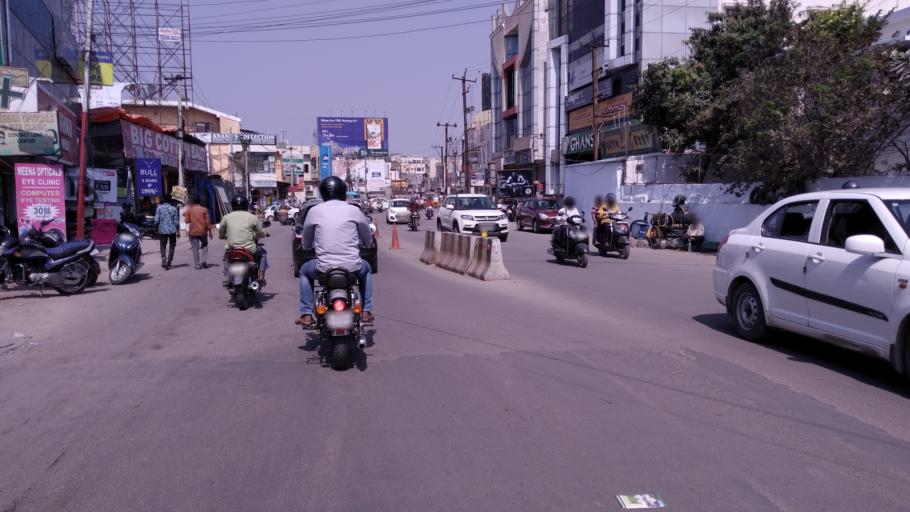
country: IN
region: Telangana
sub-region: Rangareddi
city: Quthbullapur
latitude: 17.4648
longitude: 78.4833
